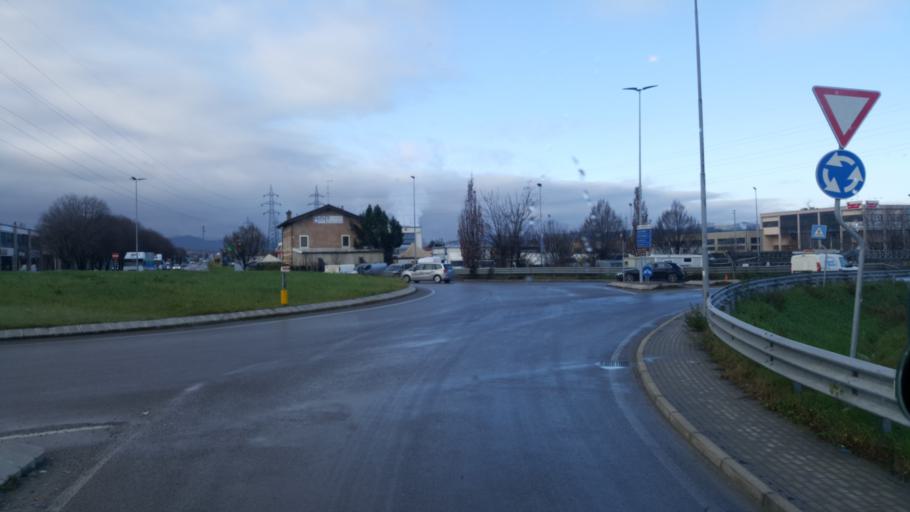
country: IT
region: Emilia-Romagna
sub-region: Provincia di Modena
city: Sassuolo
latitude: 44.5584
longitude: 10.7883
